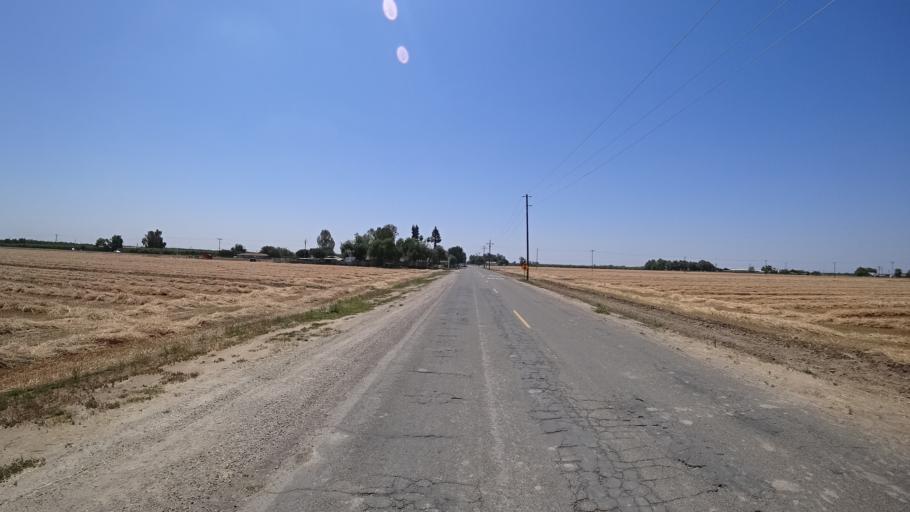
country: US
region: California
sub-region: Kings County
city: Armona
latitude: 36.2999
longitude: -119.6912
